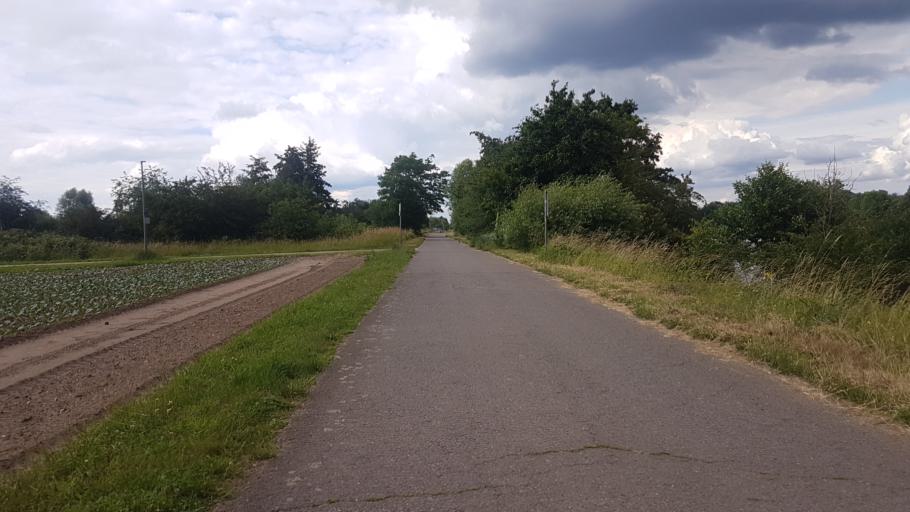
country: DE
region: Saarland
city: Ensdorf
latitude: 49.2920
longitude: 6.7646
